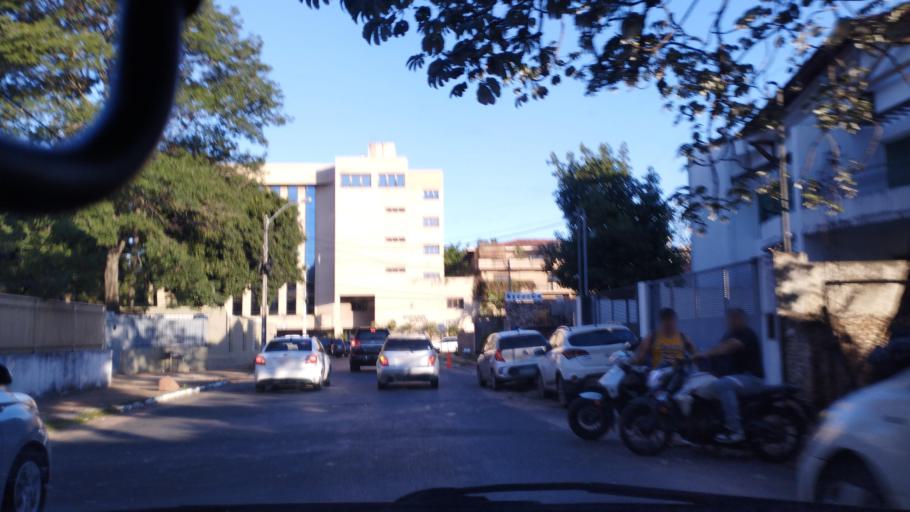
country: PY
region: Asuncion
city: Asuncion
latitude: -25.3019
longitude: -57.5886
